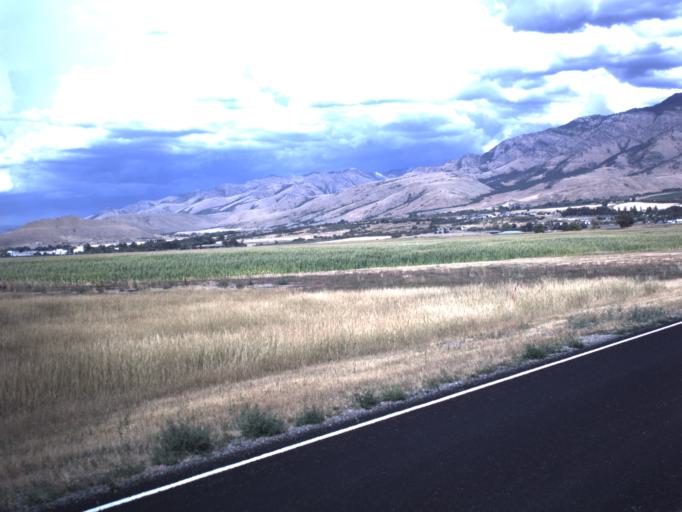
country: US
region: Utah
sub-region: Cache County
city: Richmond
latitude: 41.9230
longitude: -111.8326
